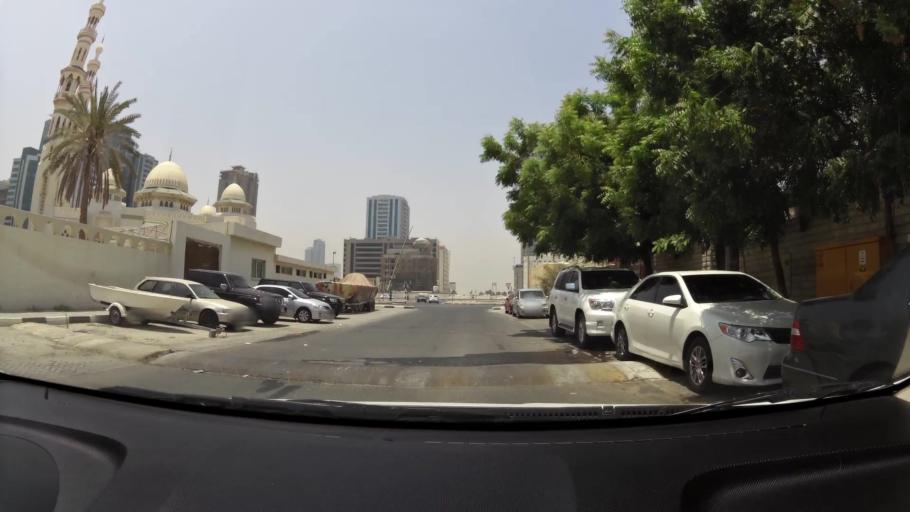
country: AE
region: Ash Shariqah
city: Sharjah
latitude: 25.3325
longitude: 55.3687
